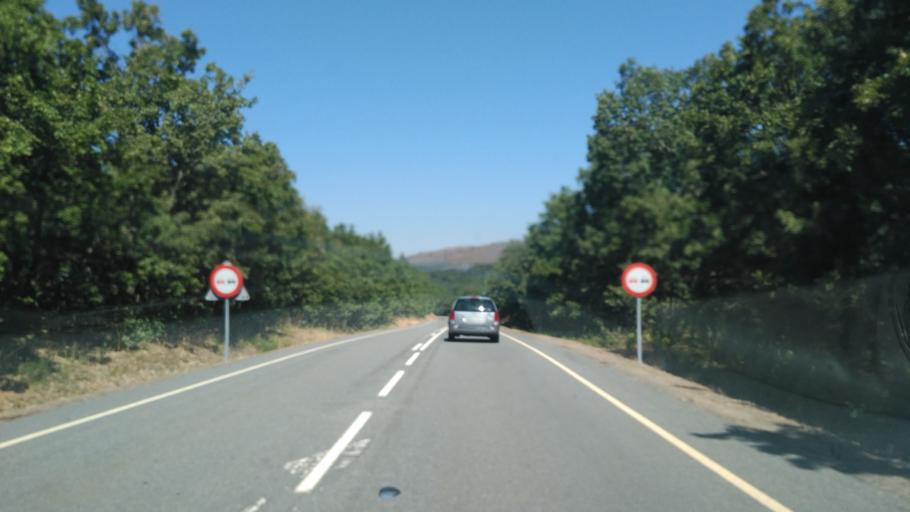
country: ES
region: Castille and Leon
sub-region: Provincia de Salamanca
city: Cilleros de la Bastida
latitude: 40.5631
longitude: -6.0702
